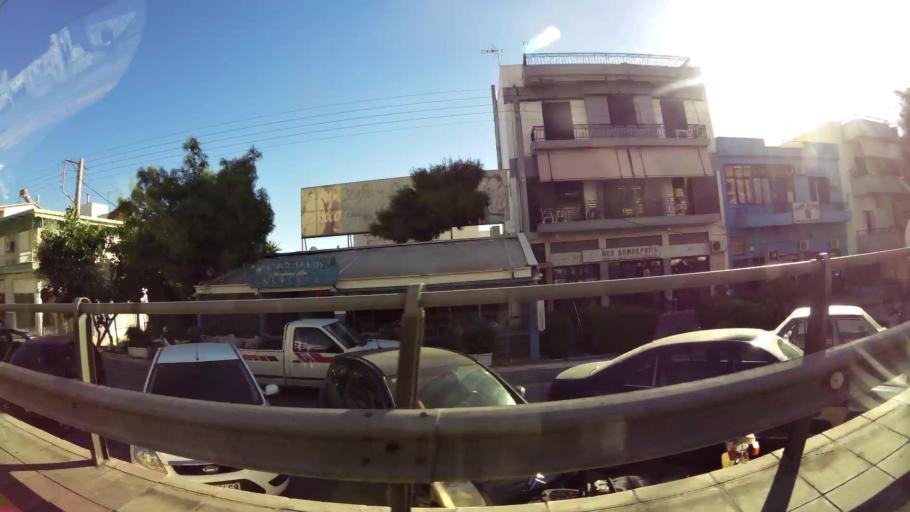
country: GR
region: Attica
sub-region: Nomos Piraios
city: Perama
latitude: 37.9639
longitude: 23.5706
